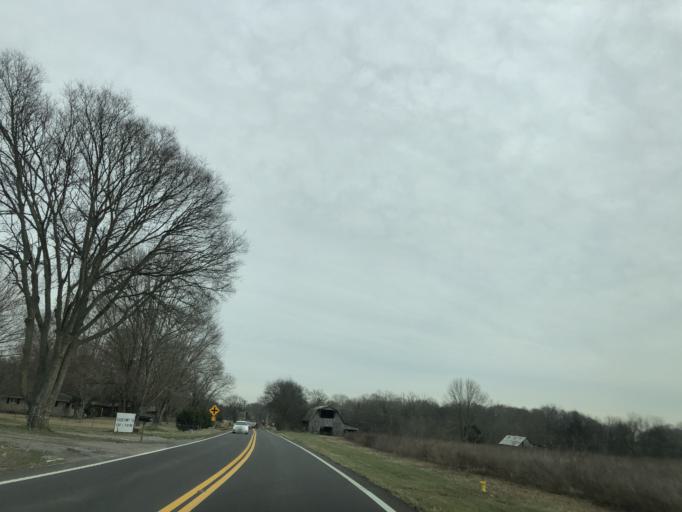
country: US
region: Tennessee
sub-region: Sumner County
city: White House
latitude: 36.4751
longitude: -86.7159
